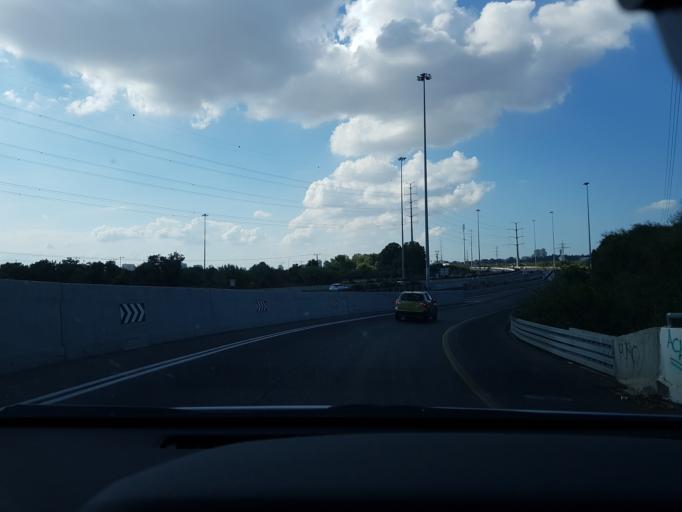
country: IL
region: Central District
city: Bet Dagan
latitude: 32.0002
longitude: 34.8038
